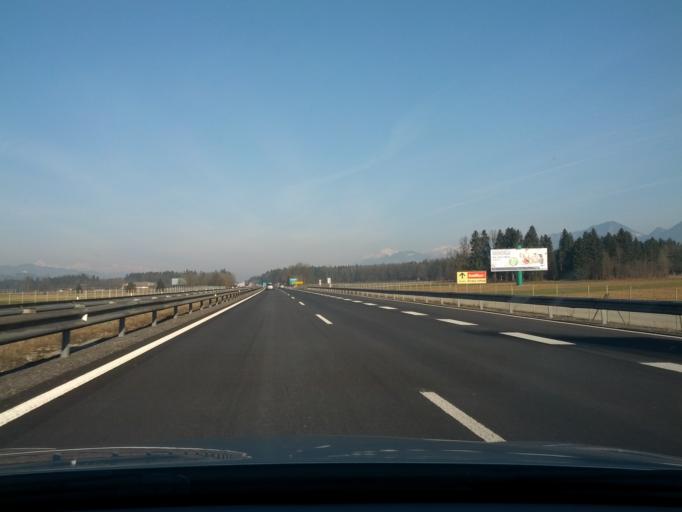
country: SI
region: Sencur
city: Sencur
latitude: 46.2169
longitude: 14.4422
